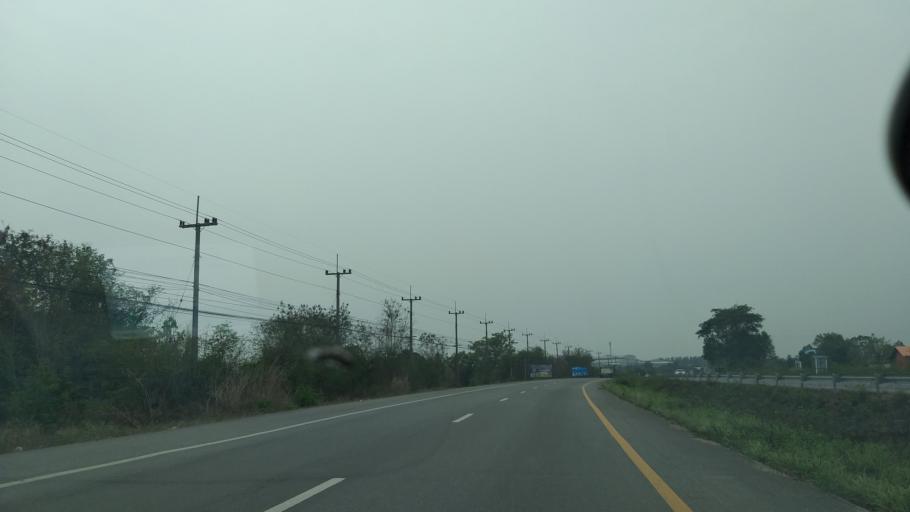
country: TH
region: Chachoengsao
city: Plaeng Yao
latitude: 13.4947
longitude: 101.2734
